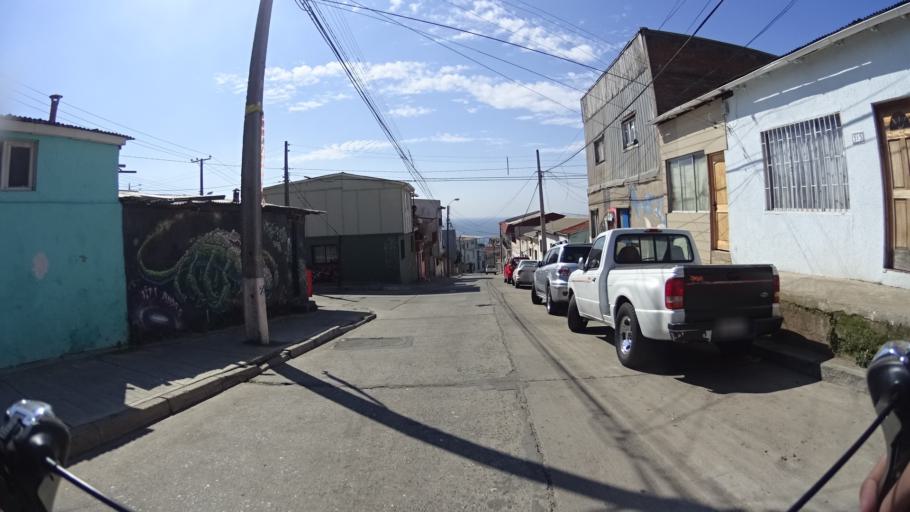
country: CL
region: Valparaiso
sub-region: Provincia de Valparaiso
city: Valparaiso
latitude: -33.0521
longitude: -71.6221
